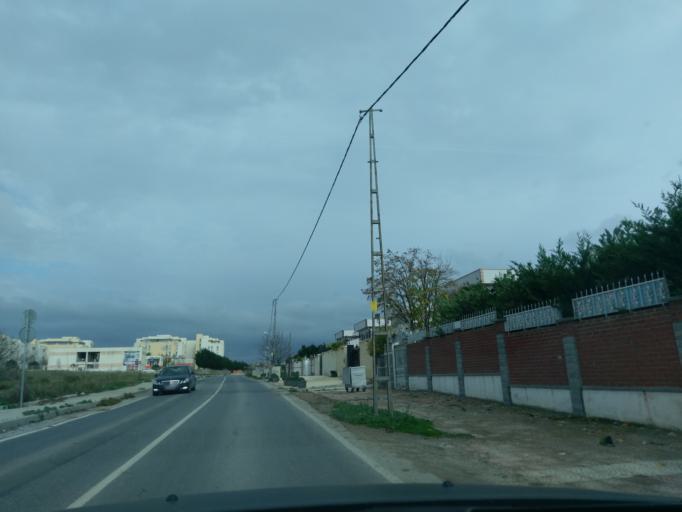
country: TR
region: Istanbul
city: Selimpasa
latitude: 41.0739
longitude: 28.3707
